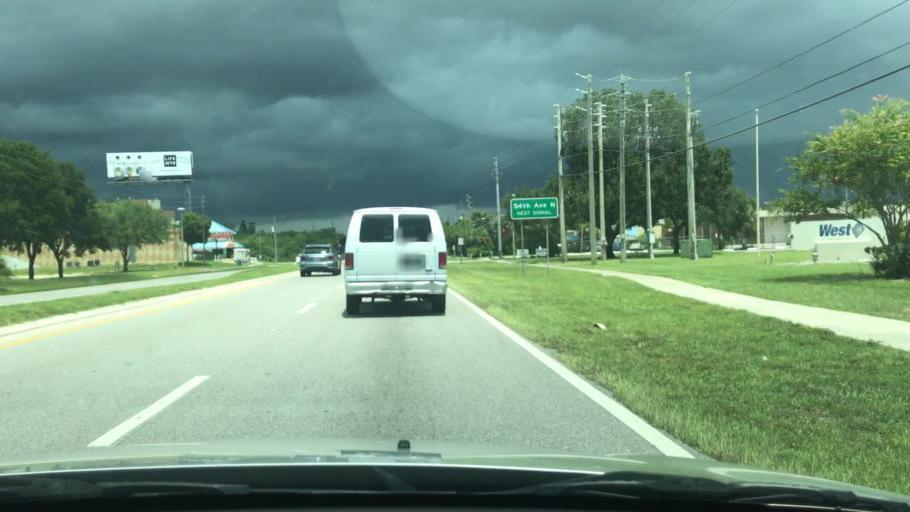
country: US
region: Florida
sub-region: Pinellas County
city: Bay Pines
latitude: 27.8177
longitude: -82.7538
